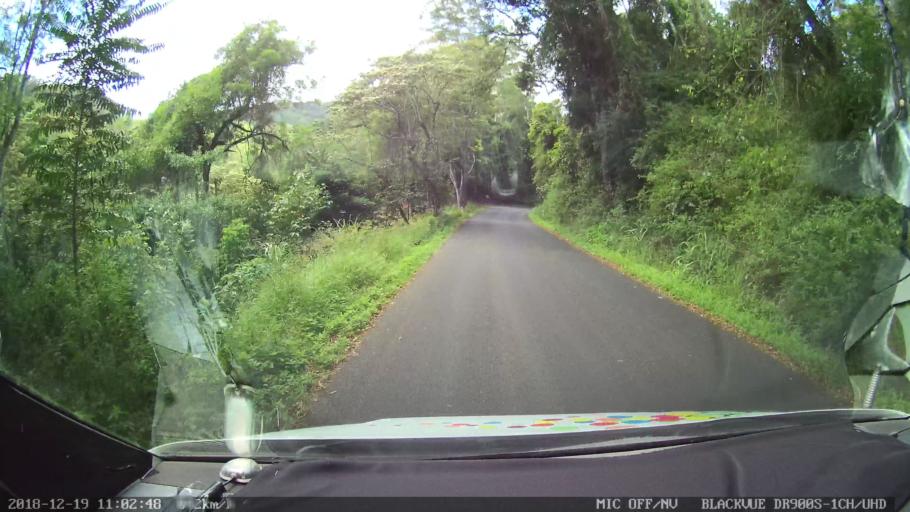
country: AU
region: New South Wales
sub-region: Lismore Municipality
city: Nimbin
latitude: -28.6076
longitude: 153.2695
